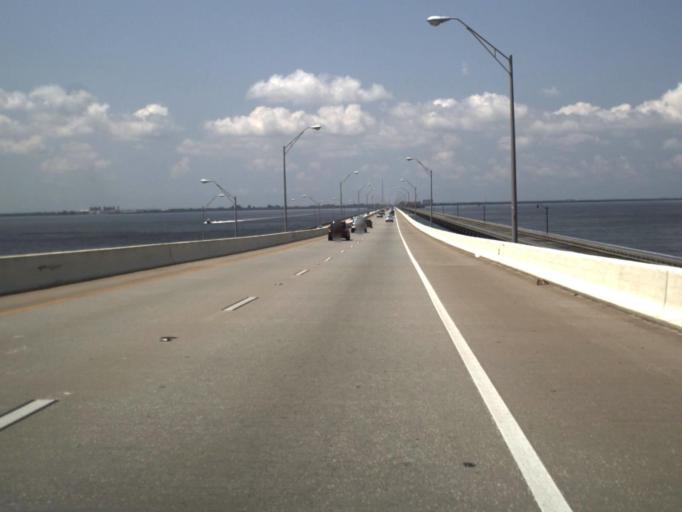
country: US
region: Florida
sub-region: Pinellas County
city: Gandy
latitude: 27.8868
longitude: -82.5560
